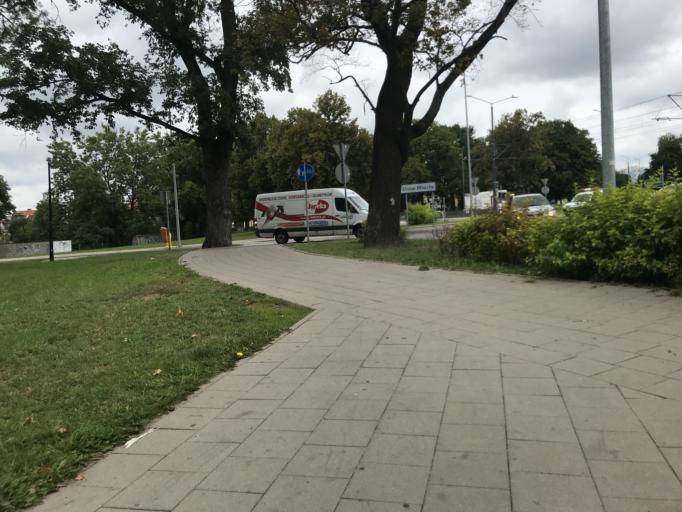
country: PL
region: Warmian-Masurian Voivodeship
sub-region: Powiat elblaski
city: Elblag
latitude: 54.1656
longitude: 19.3988
